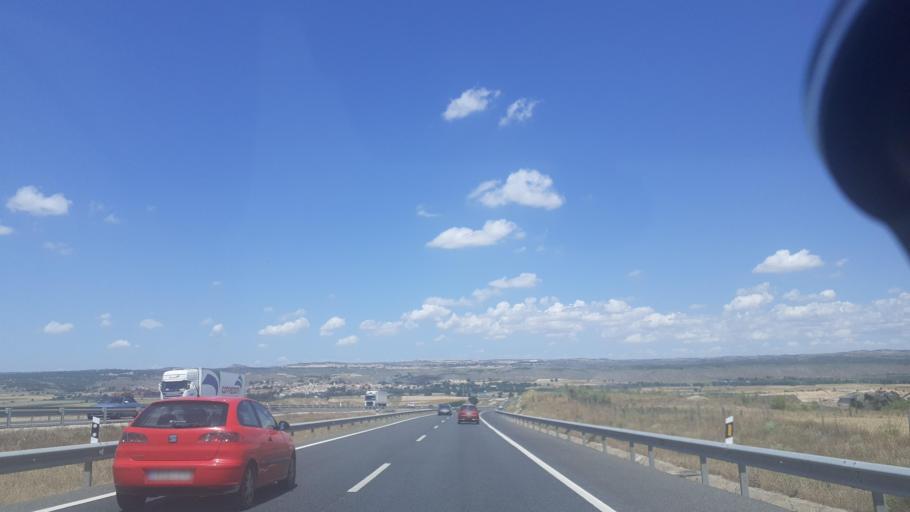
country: ES
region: Madrid
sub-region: Provincia de Madrid
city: Fuentiduena de Tajo
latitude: 40.1013
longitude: -3.1350
